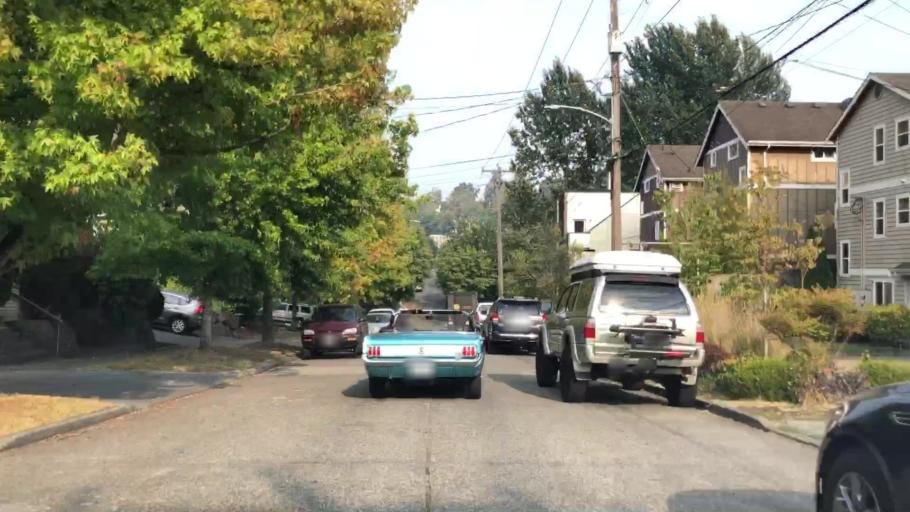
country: US
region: Washington
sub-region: King County
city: White Center
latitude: 47.5654
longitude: -122.3692
